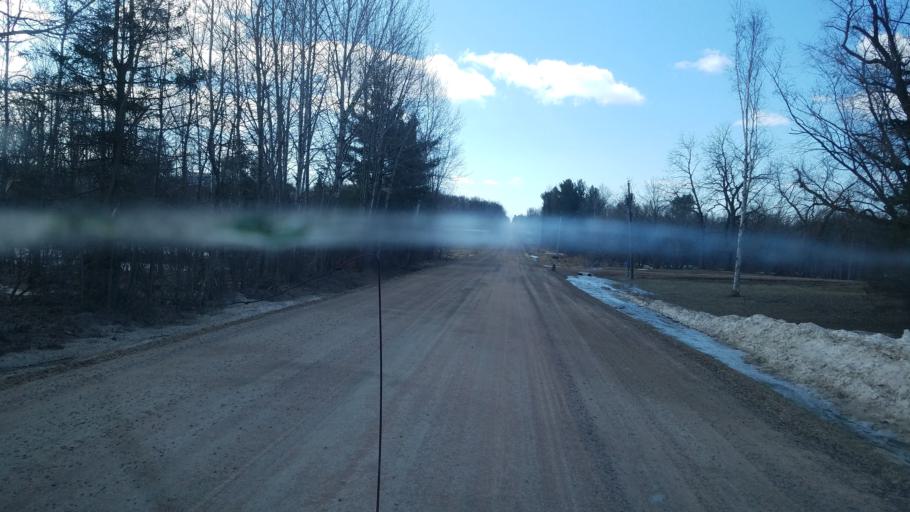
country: US
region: Wisconsin
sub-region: Clark County
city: Loyal
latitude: 44.6796
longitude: -90.4558
